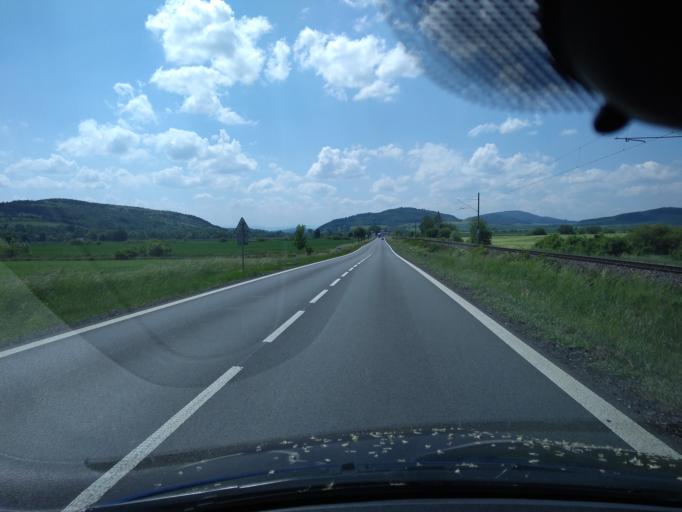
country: CZ
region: Plzensky
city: Prestice
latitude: 49.5408
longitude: 13.3094
